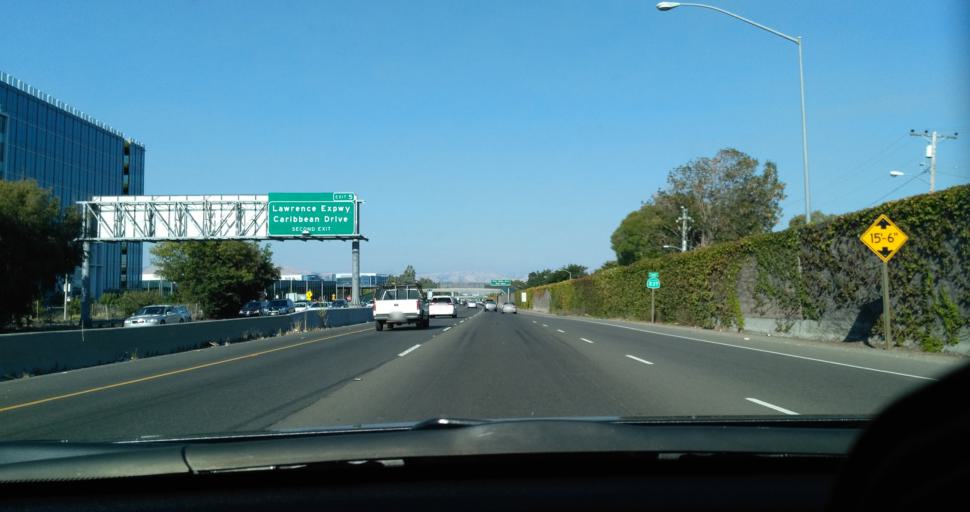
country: US
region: California
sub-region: Santa Clara County
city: Sunnyvale
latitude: 37.4038
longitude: -122.0229
